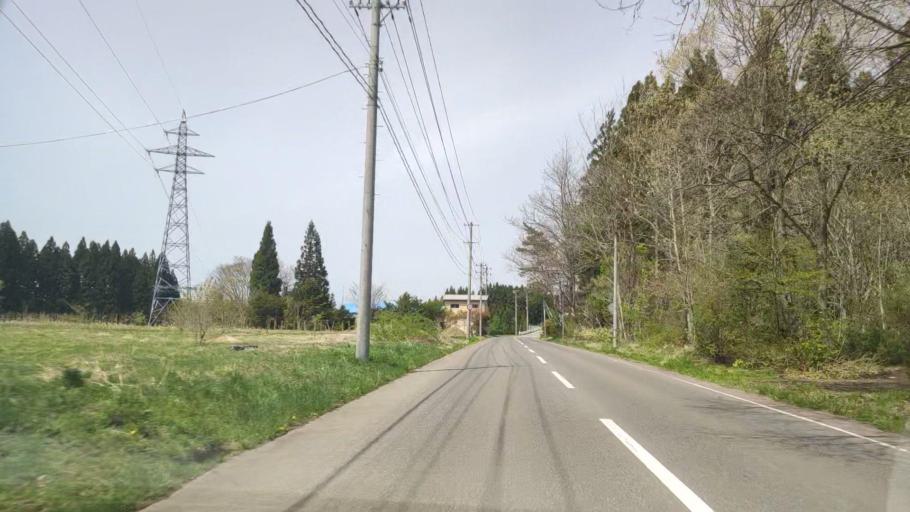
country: JP
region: Aomori
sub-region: Misawa Shi
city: Inuotose
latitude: 40.7221
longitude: 141.1416
